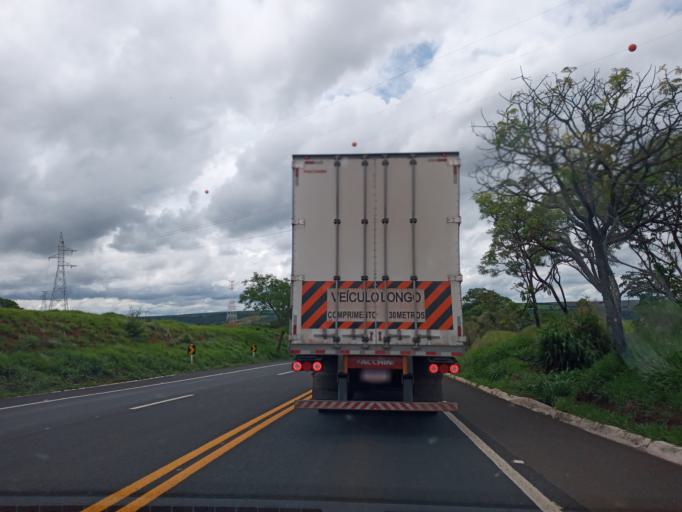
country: BR
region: Minas Gerais
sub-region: Uberaba
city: Uberaba
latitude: -19.2871
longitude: -47.6221
